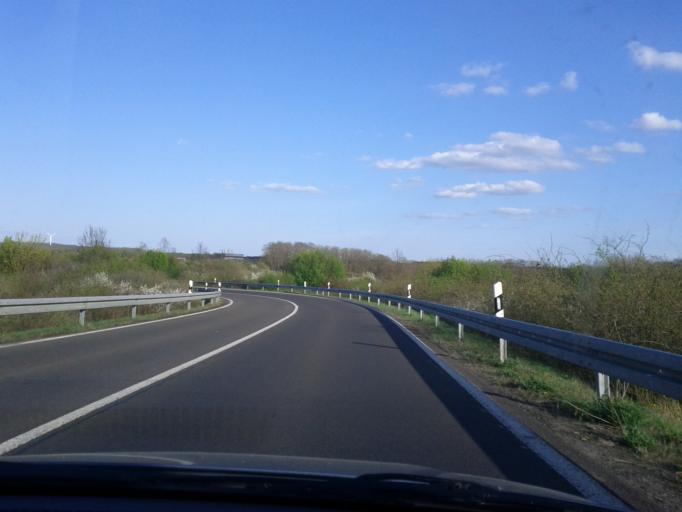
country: DE
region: Brandenburg
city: Woltersdorf
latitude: 52.4761
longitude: 13.7576
